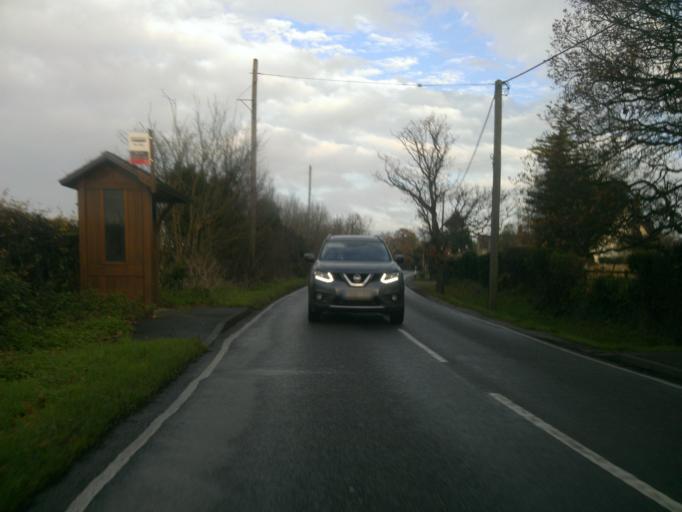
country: GB
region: England
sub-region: Essex
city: Wivenhoe
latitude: 51.8562
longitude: 0.9767
